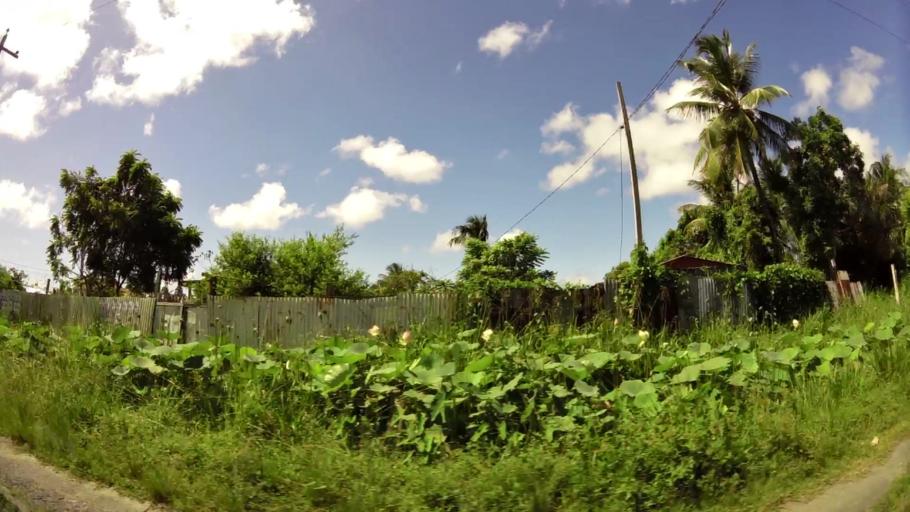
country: GY
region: Demerara-Mahaica
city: Georgetown
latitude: 6.7854
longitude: -58.1371
